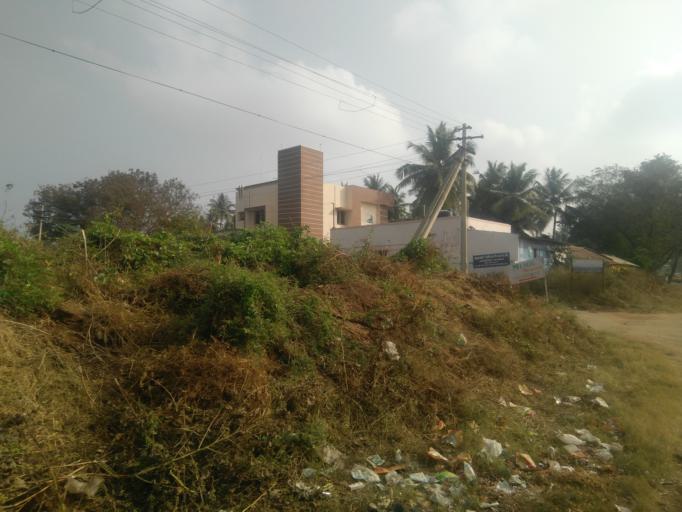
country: IN
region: Tamil Nadu
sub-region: Coimbatore
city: Coimbatore
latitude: 11.0662
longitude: 76.9179
